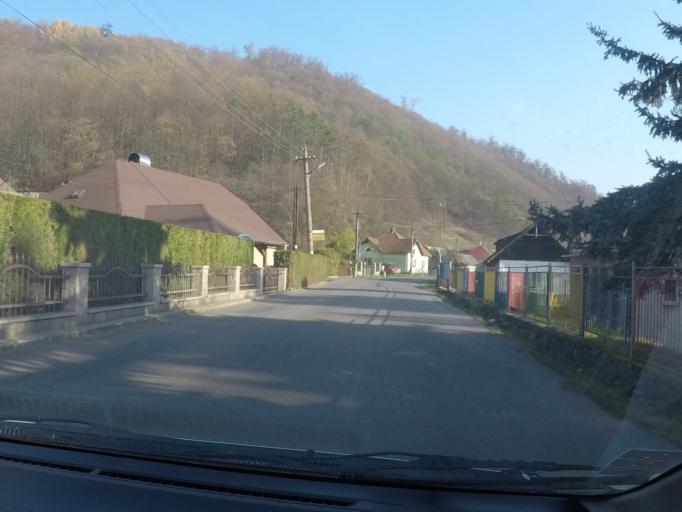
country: SK
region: Banskobystricky
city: Zarnovica
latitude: 48.4607
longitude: 18.7630
